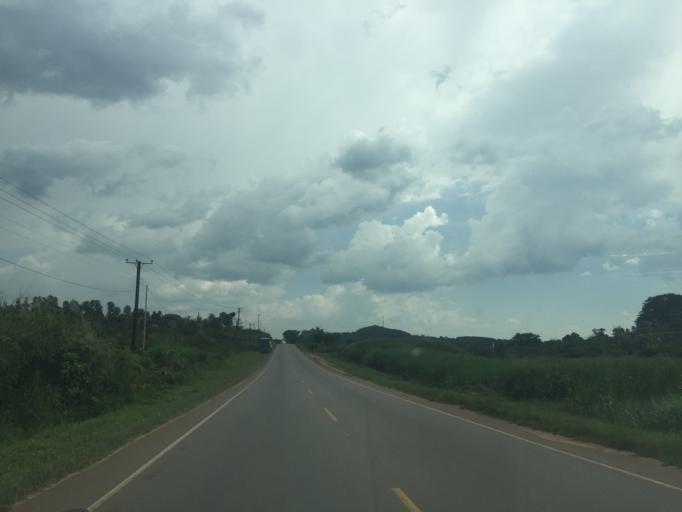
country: UG
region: Central Region
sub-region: Luwero District
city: Wobulenzi
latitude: 0.6646
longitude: 32.5294
